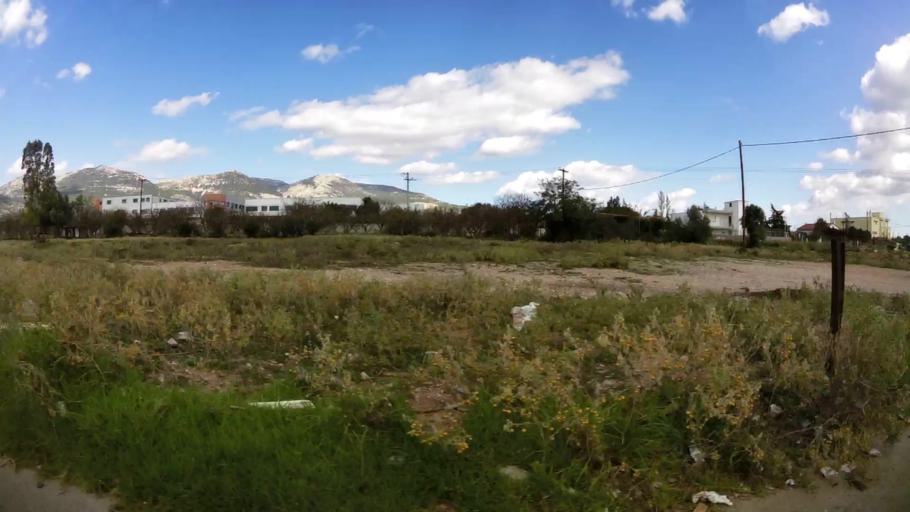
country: GR
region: Attica
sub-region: Nomarchia Anatolikis Attikis
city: Thrakomakedones
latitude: 38.1060
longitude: 23.7586
